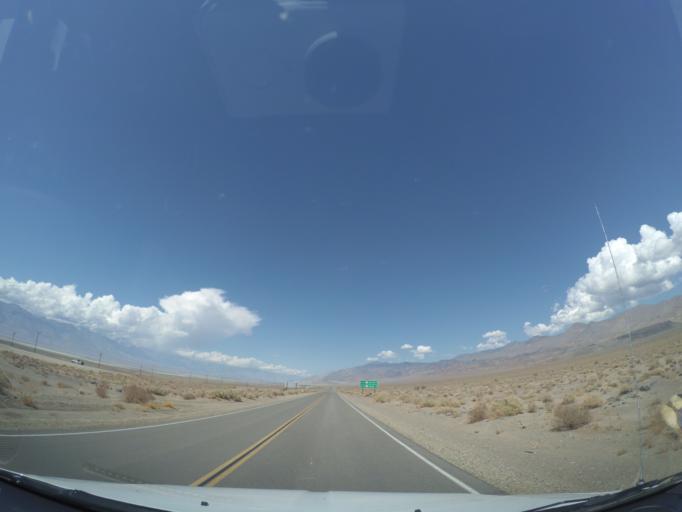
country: US
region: California
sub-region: Inyo County
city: Lone Pine
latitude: 36.4291
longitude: -117.8238
